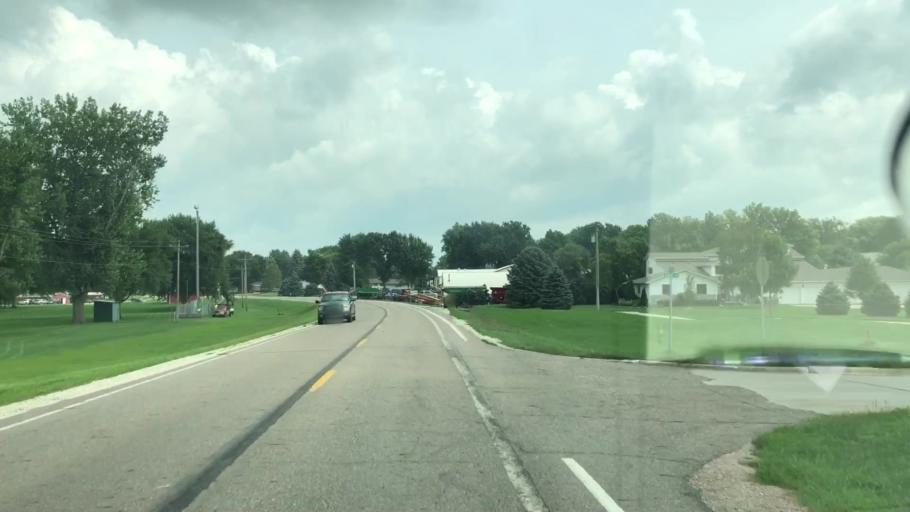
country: US
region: Iowa
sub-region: Plymouth County
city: Kingsley
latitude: 42.5829
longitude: -95.9739
